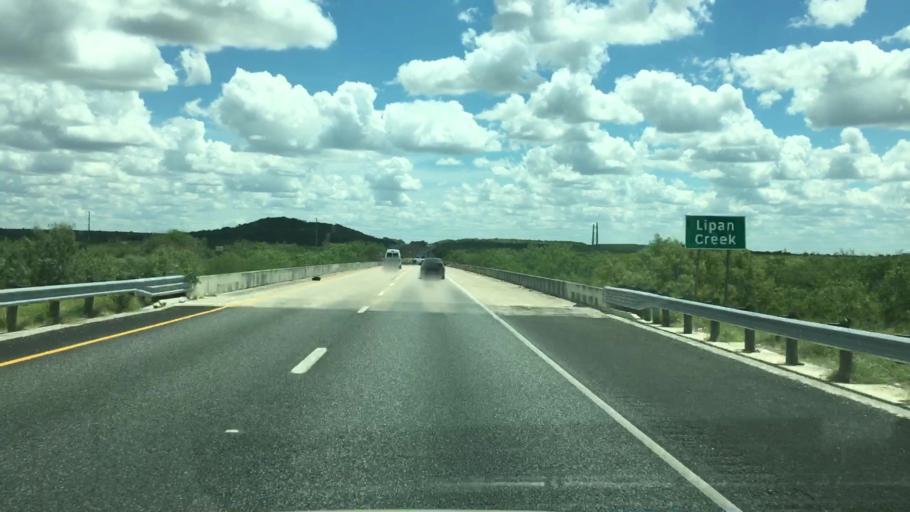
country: US
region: Texas
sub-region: Live Oak County
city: Three Rivers
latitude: 28.7323
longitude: -98.2889
